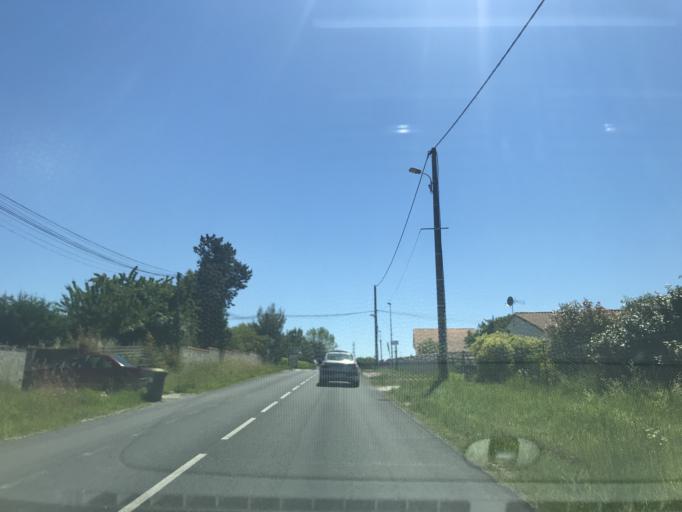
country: FR
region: Poitou-Charentes
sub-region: Departement de la Charente-Maritime
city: Meschers-sur-Gironde
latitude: 45.5759
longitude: -0.9606
